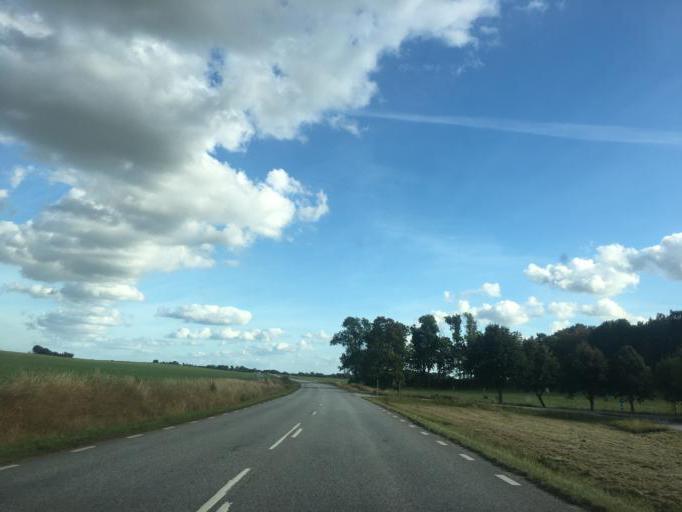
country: SE
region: Skane
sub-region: Eslovs Kommun
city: Eslov
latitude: 55.7613
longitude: 13.3279
